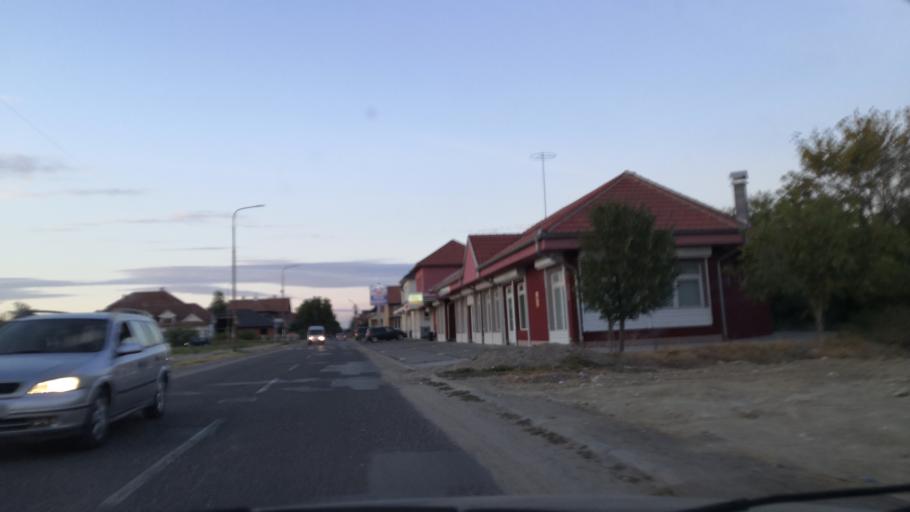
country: RS
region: Central Serbia
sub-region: Borski Okrug
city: Negotin
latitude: 44.2352
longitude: 22.5294
